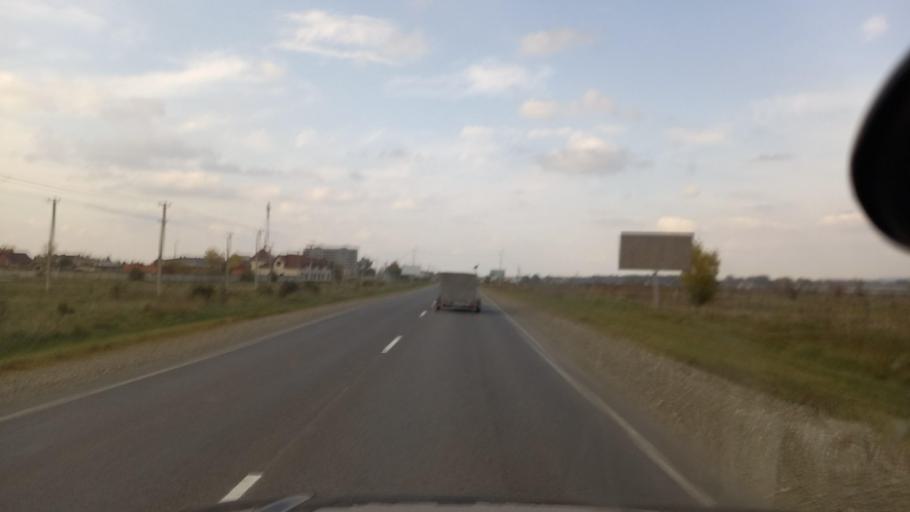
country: RU
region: Krasnodarskiy
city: Mostovskoy
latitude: 44.3871
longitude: 40.8175
